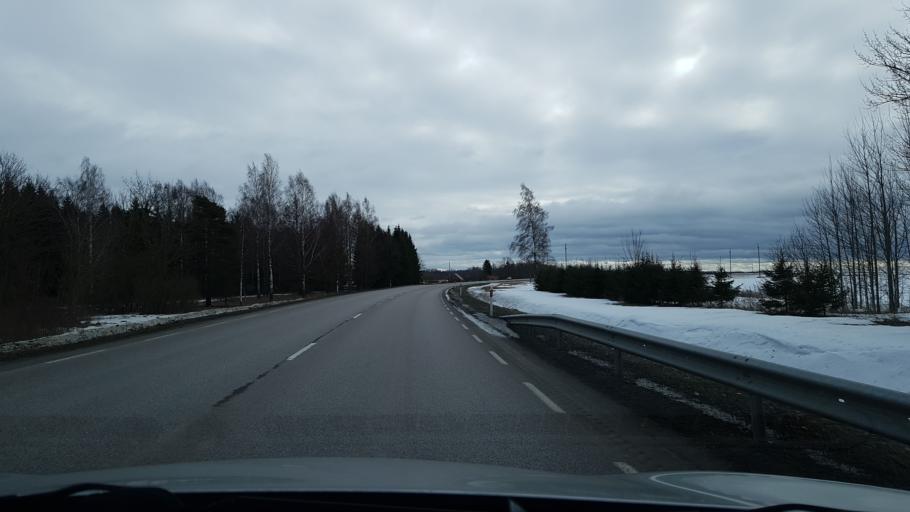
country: EE
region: Jogevamaa
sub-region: Jogeva linn
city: Jogeva
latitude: 58.7250
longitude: 26.3917
